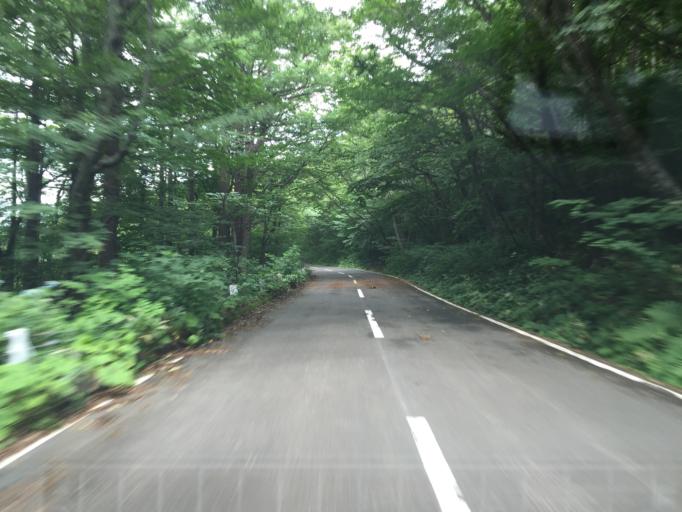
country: JP
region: Fukushima
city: Nihommatsu
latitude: 37.6576
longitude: 140.3204
